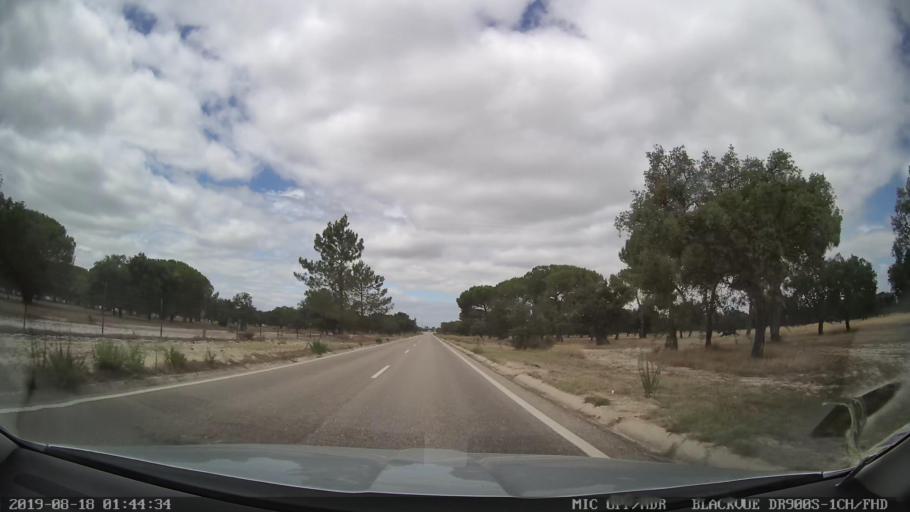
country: PT
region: Santarem
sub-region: Benavente
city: Poceirao
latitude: 38.9071
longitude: -8.7611
